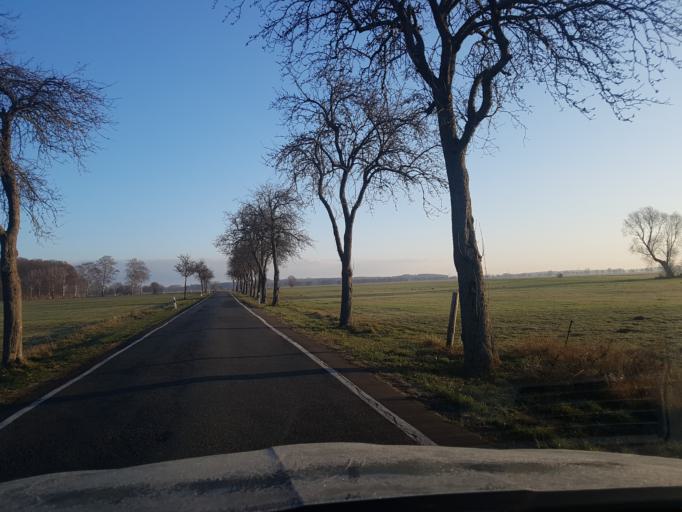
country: DE
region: Brandenburg
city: Schlieben
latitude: 51.7028
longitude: 13.3430
